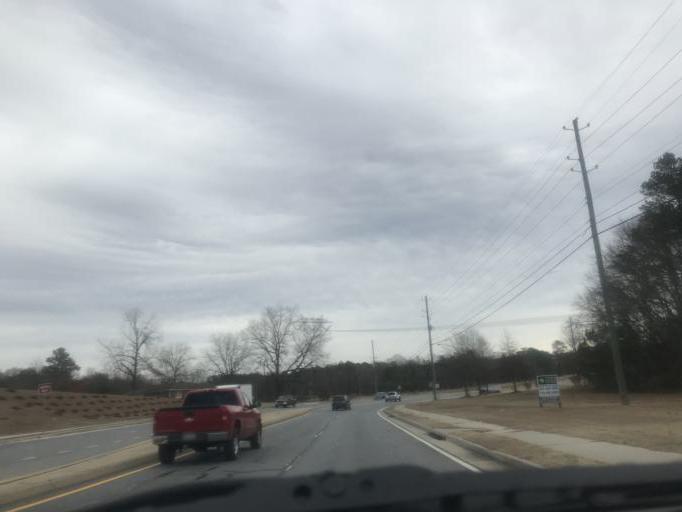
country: US
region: Georgia
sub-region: Gwinnett County
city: Buford
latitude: 34.0703
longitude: -83.9630
